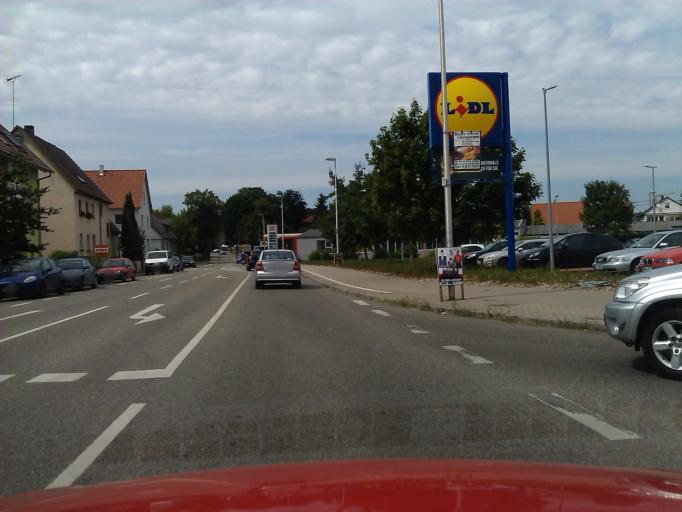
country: DE
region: Baden-Wuerttemberg
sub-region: Regierungsbezirk Stuttgart
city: Leingarten
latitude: 49.1463
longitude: 9.1196
